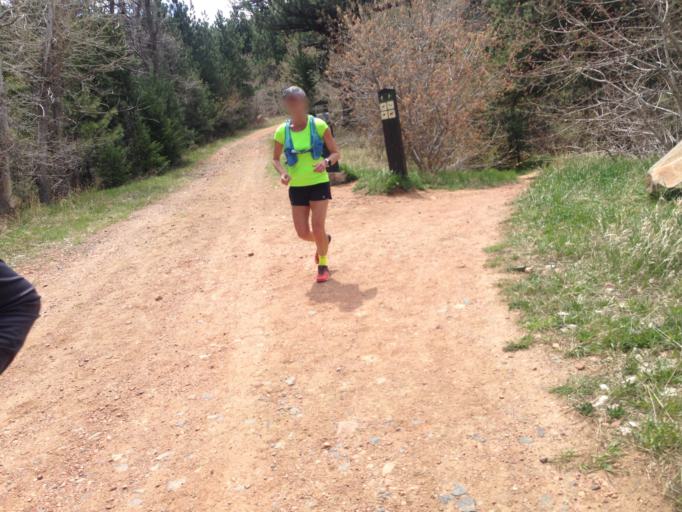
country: US
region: Colorado
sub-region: Boulder County
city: Boulder
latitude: 39.9267
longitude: -105.2763
